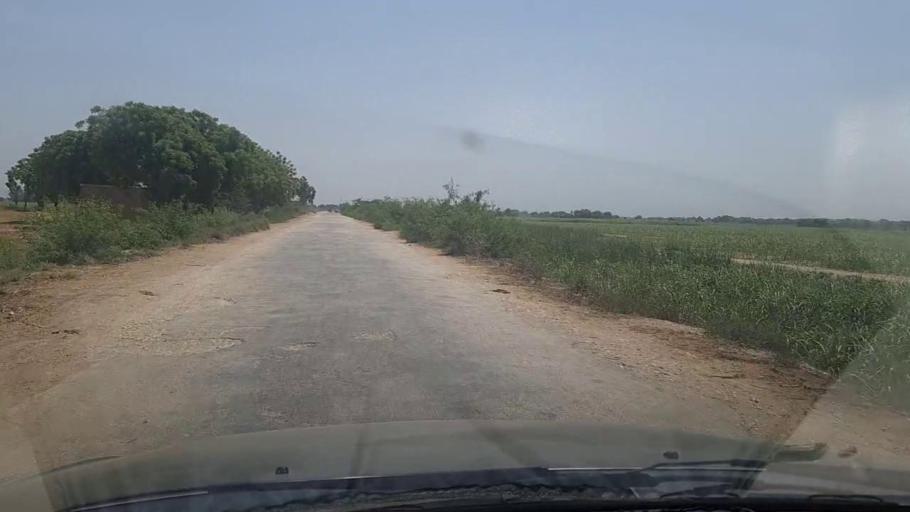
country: PK
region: Sindh
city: Tando Muhammad Khan
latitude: 25.2715
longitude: 68.6321
